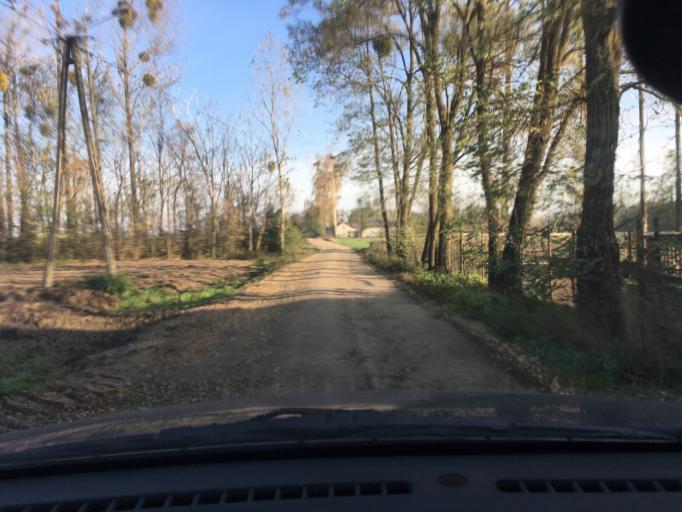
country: PL
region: Masovian Voivodeship
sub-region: Powiat plocki
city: Mala Wies
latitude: 52.4431
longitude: 20.1072
